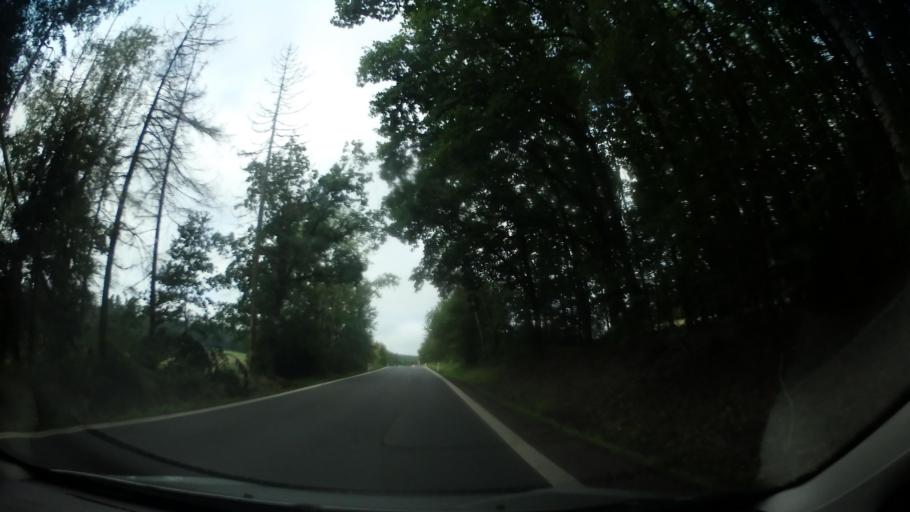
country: CZ
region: Central Bohemia
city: Neveklov
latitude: 49.7517
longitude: 14.5702
